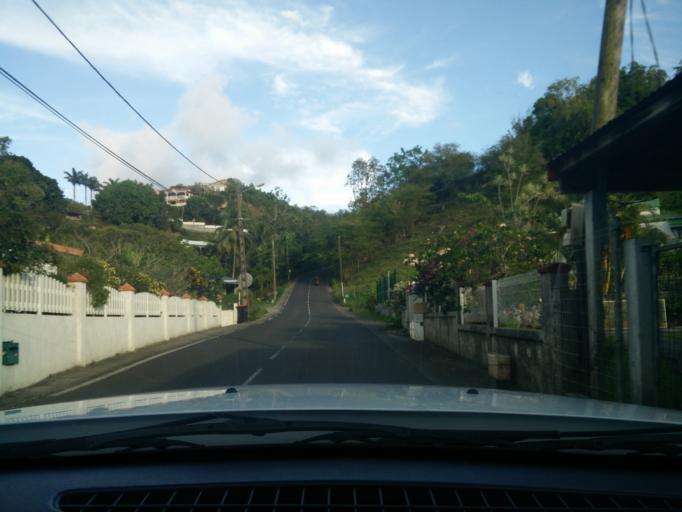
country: GP
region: Guadeloupe
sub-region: Guadeloupe
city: Les Abymes
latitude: 16.2475
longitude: -61.4931
